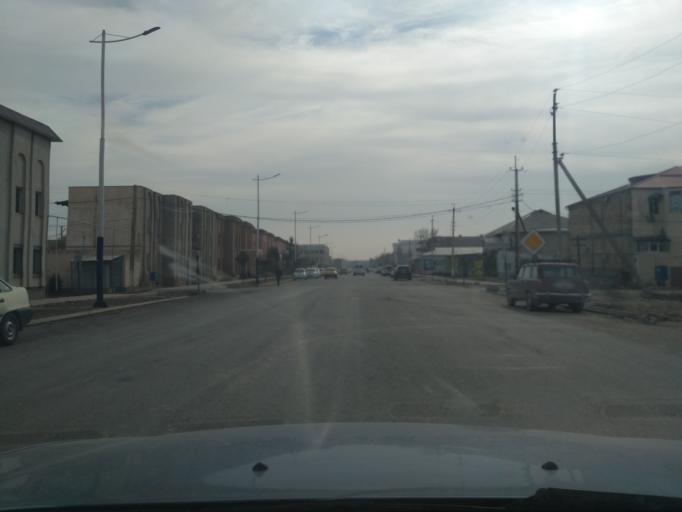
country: UZ
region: Sirdaryo
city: Guliston
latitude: 40.5009
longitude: 68.7721
